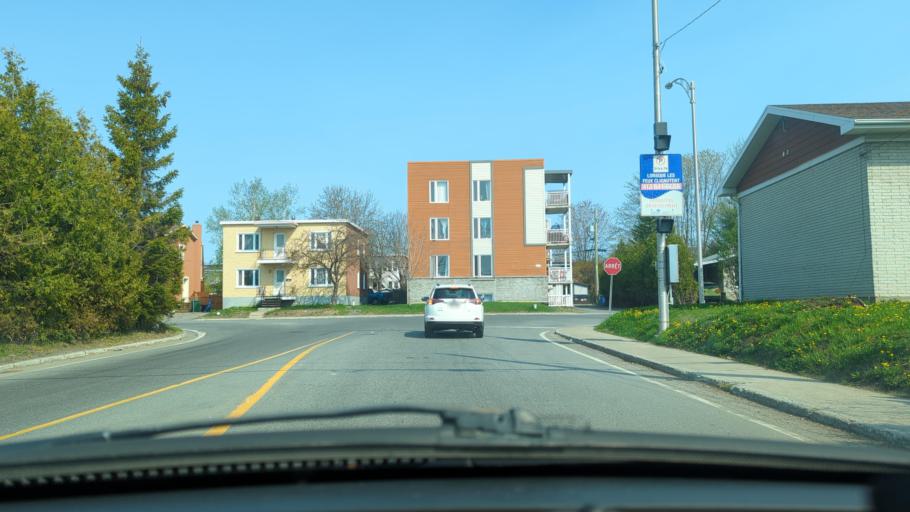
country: CA
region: Quebec
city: Quebec
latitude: 46.8460
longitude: -71.2474
